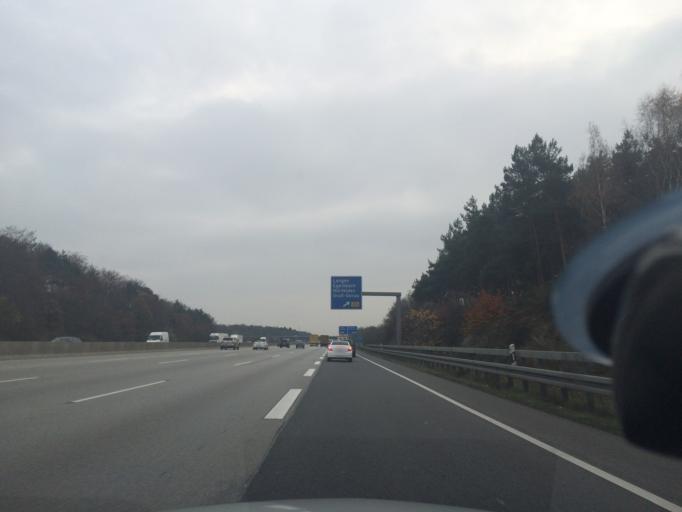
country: DE
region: Hesse
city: Morfelden-Walldorf
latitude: 49.9887
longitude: 8.5998
